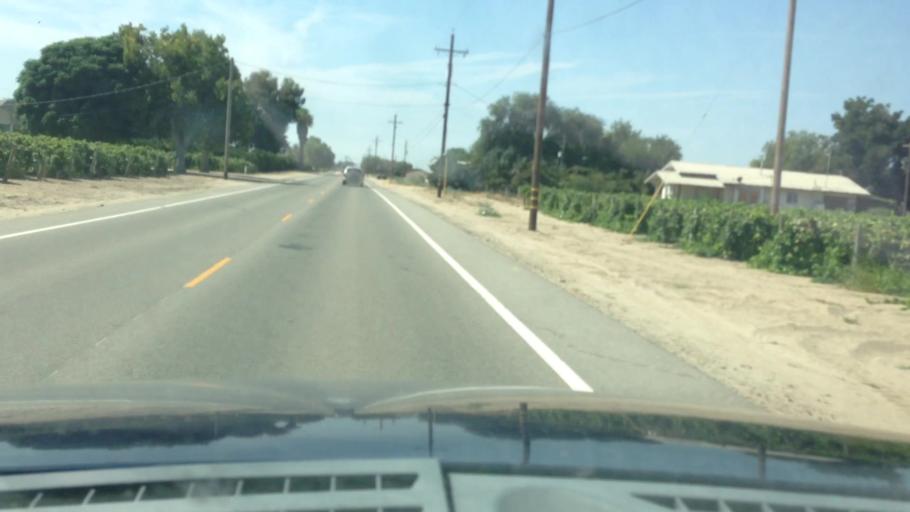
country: US
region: California
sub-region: Fresno County
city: Kingsburg
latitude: 36.5535
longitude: -119.5566
